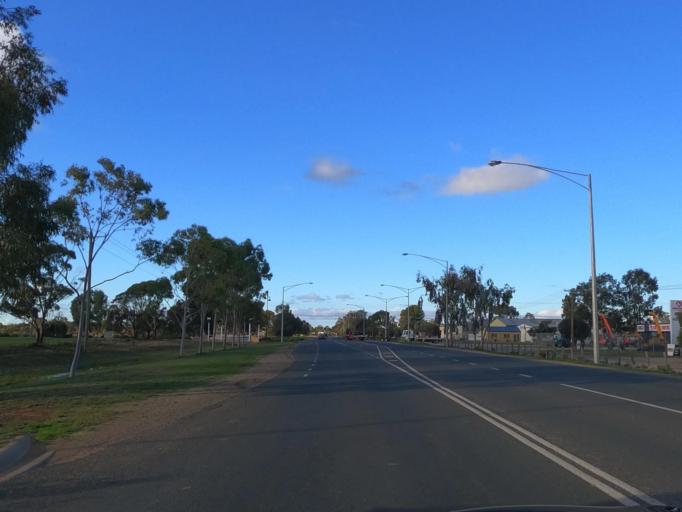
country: AU
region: Victoria
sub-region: Swan Hill
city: Swan Hill
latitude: -35.3421
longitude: 143.5342
